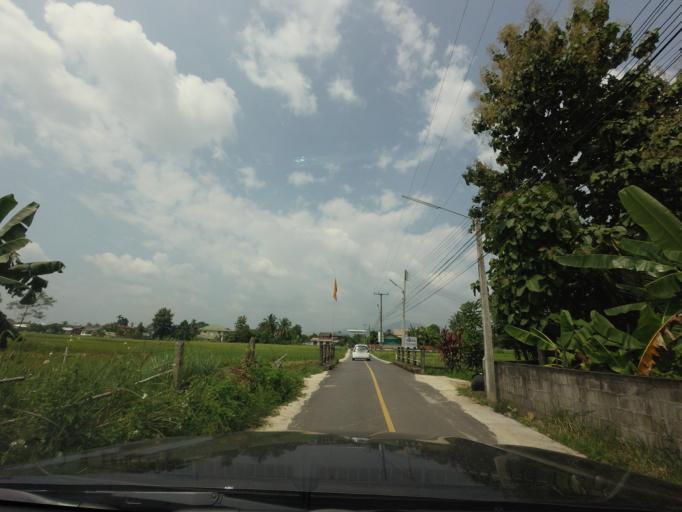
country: TH
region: Nan
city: Pua
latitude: 19.1729
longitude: 100.9377
